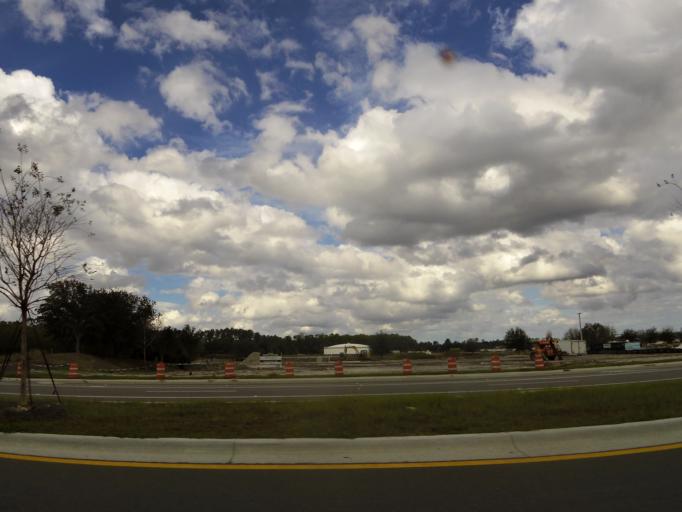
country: US
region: Florida
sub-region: Saint Johns County
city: Villano Beach
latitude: 29.9880
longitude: -81.4548
